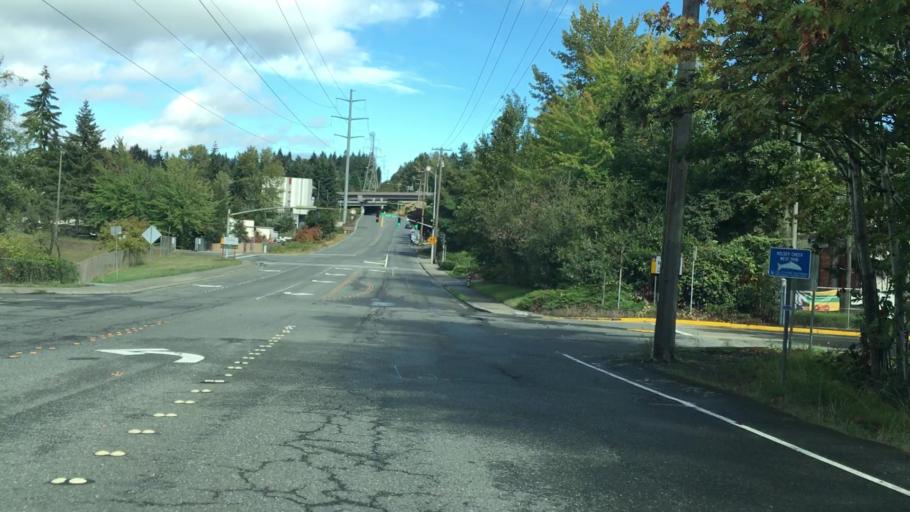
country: US
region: Washington
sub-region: King County
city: Bellevue
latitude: 47.6264
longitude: -122.1751
